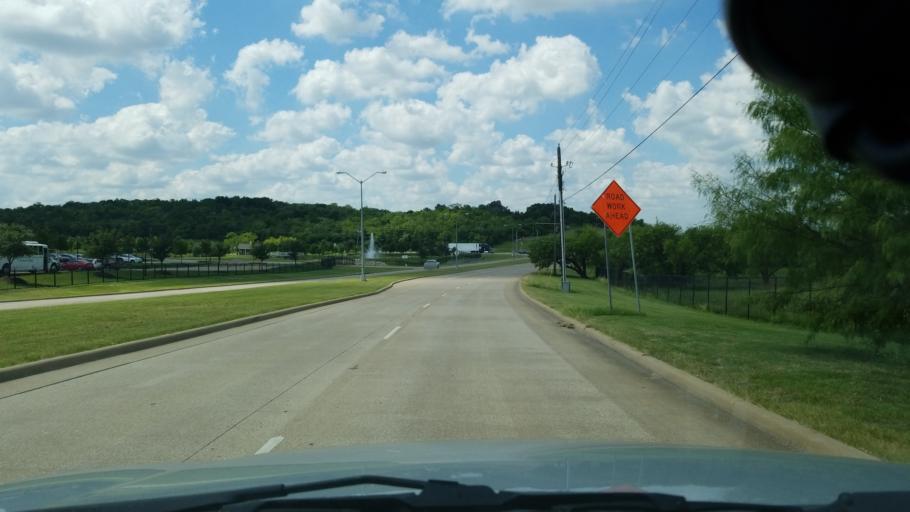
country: US
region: Texas
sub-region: Dallas County
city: Grand Prairie
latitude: 32.7094
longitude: -96.9519
